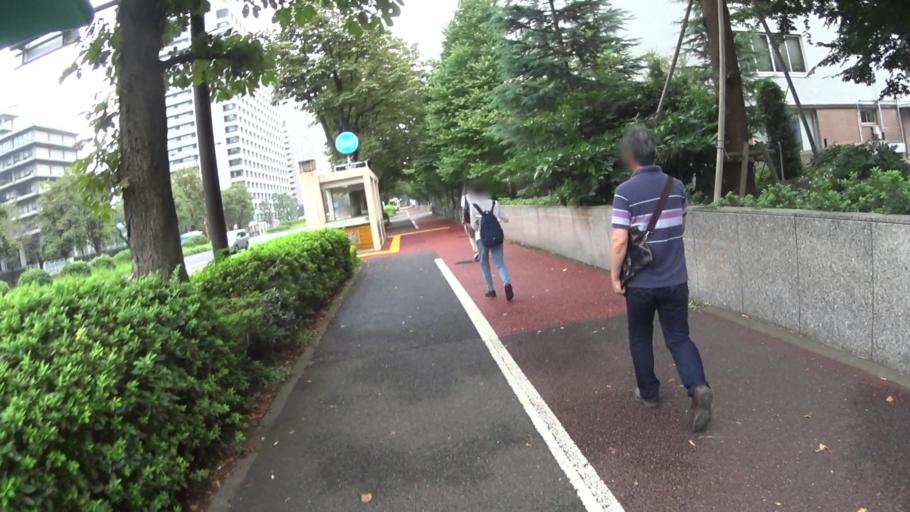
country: JP
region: Tokyo
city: Tokyo
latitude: 35.6734
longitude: 139.7517
